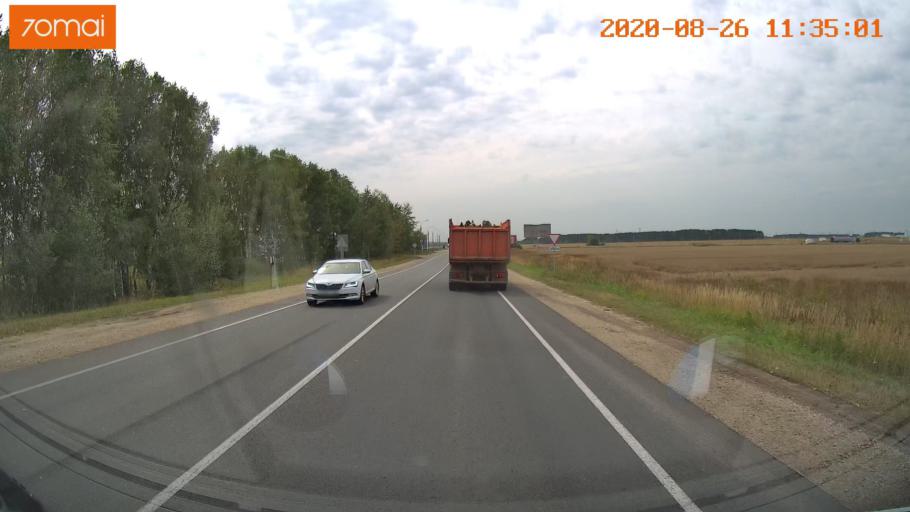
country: RU
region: Rjazan
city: Shilovo
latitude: 54.2789
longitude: 40.8379
